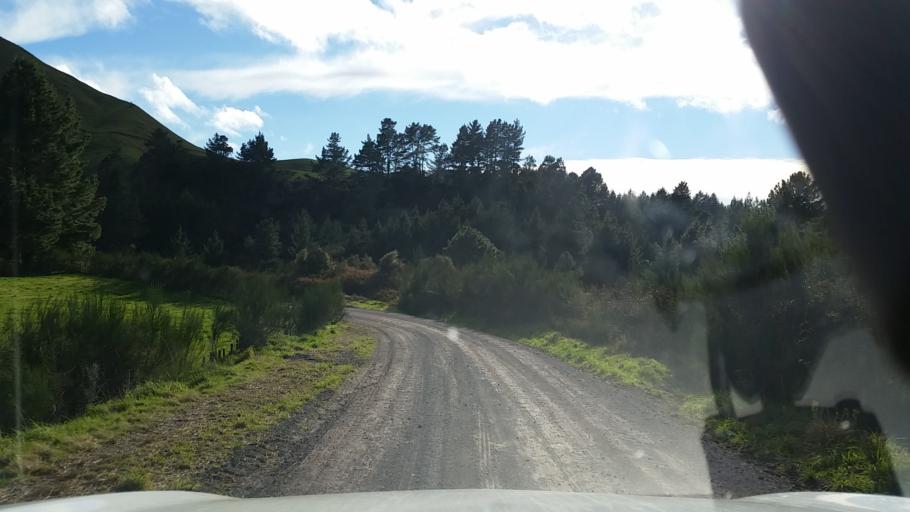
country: NZ
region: Bay of Plenty
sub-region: Rotorua District
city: Rotorua
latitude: -38.3788
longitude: 176.2022
